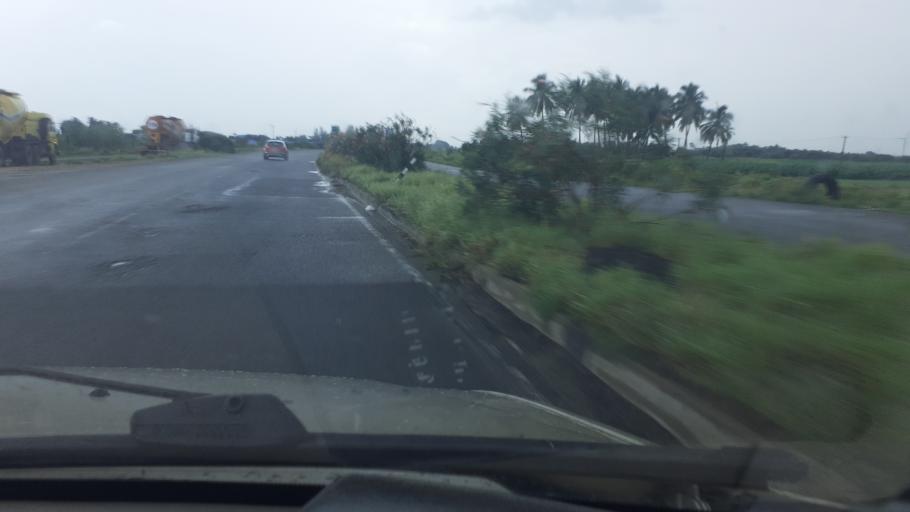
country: IN
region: Tamil Nadu
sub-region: Thoothukkudi
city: Kadambur
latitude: 9.0314
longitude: 77.7890
